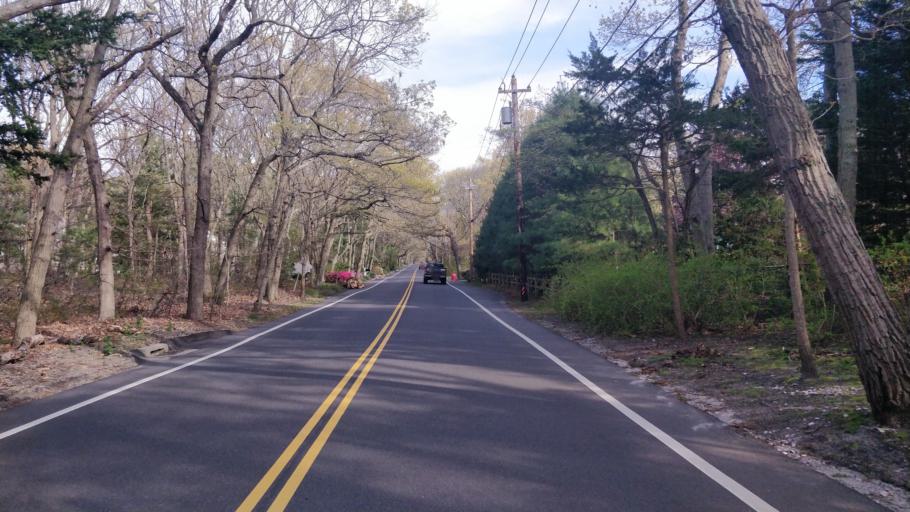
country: US
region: New York
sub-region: Suffolk County
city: Stony Brook
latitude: 40.9431
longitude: -73.1353
